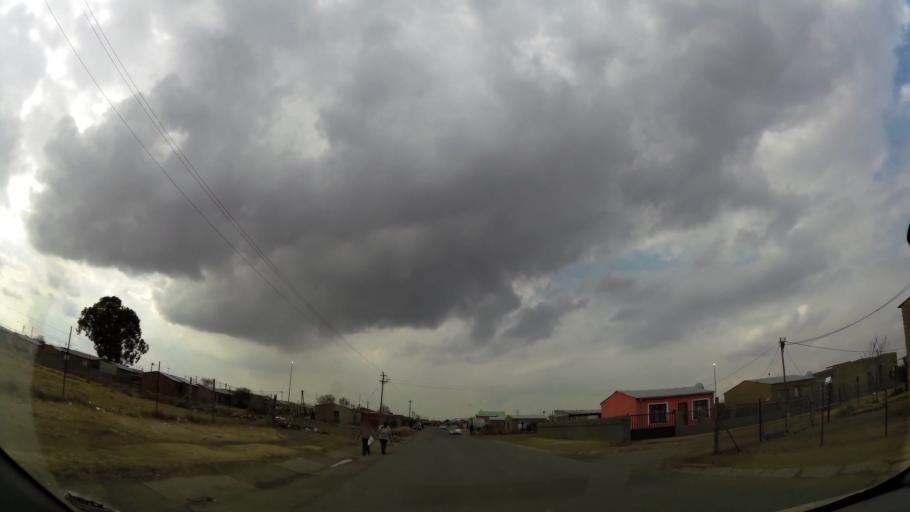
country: ZA
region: Orange Free State
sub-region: Fezile Dabi District Municipality
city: Sasolburg
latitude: -26.8532
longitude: 27.8605
